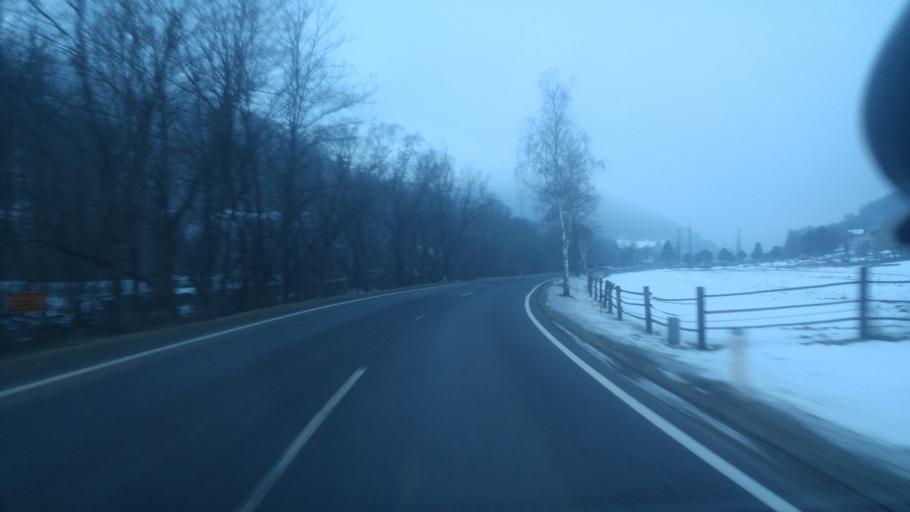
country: AT
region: Lower Austria
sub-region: Politischer Bezirk Baden
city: Altenmarkt an der Triesting
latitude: 48.0042
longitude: 16.0203
